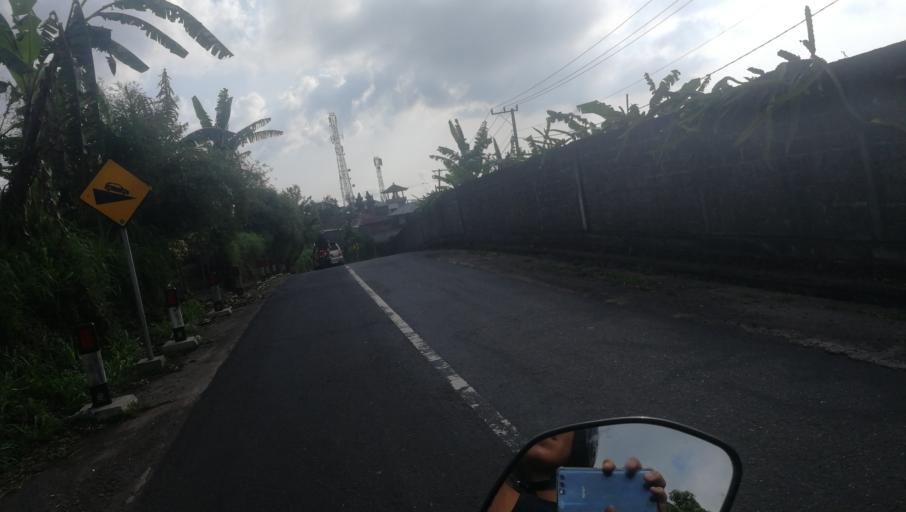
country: ID
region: Bali
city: Munduk
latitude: -8.2612
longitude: 115.0889
